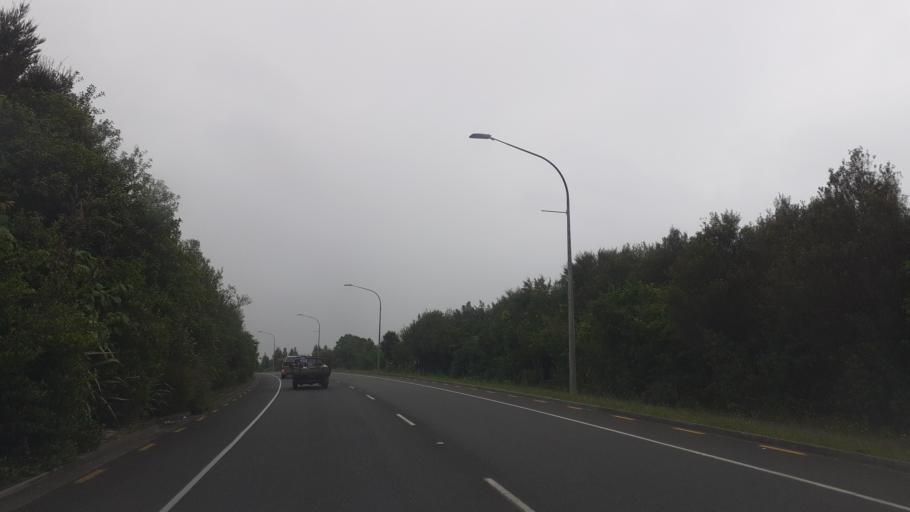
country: NZ
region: Northland
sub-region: Far North District
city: Kerikeri
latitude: -35.2145
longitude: 173.9525
